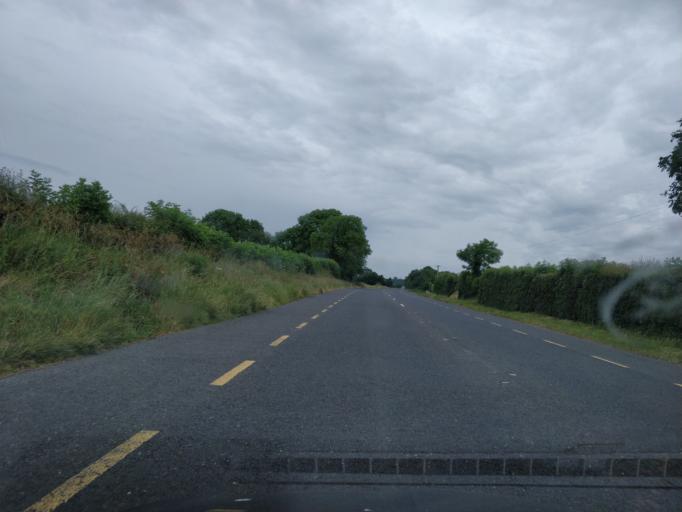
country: IE
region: Munster
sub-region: North Tipperary
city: Roscrea
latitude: 52.9517
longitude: -7.6909
